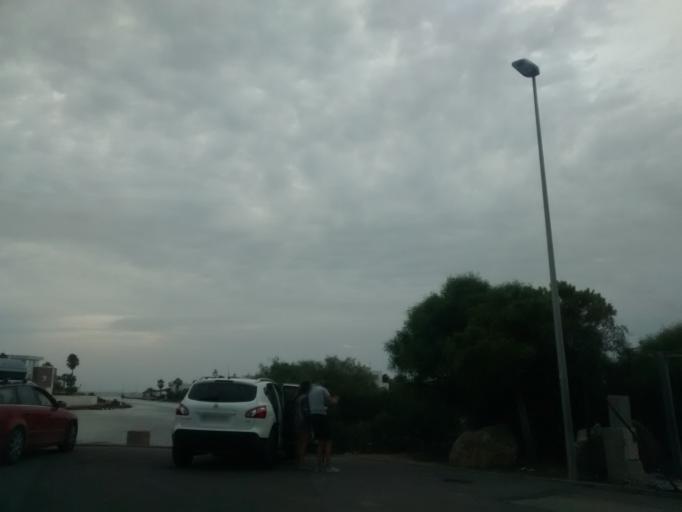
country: ES
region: Murcia
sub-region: Murcia
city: San Pedro del Pinatar
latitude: 37.7781
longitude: -0.7501
